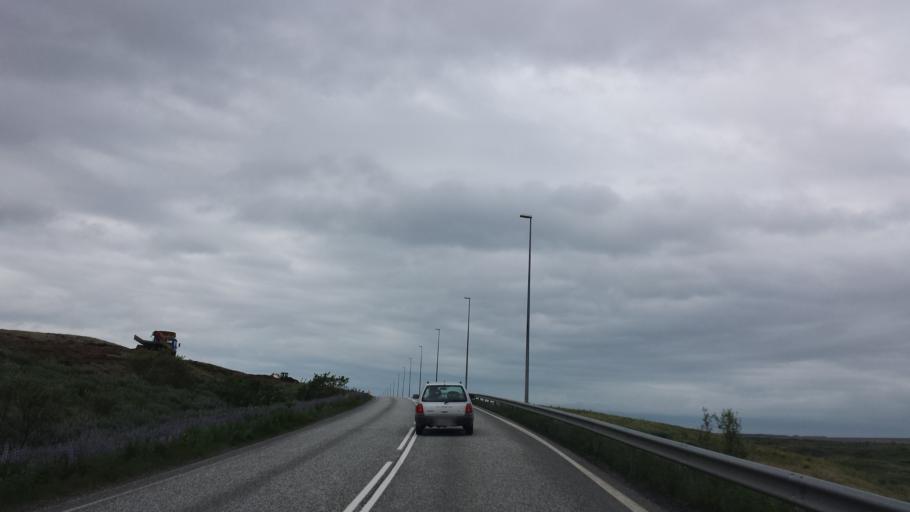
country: IS
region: Capital Region
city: Mosfellsbaer
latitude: 64.1798
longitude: -21.6533
